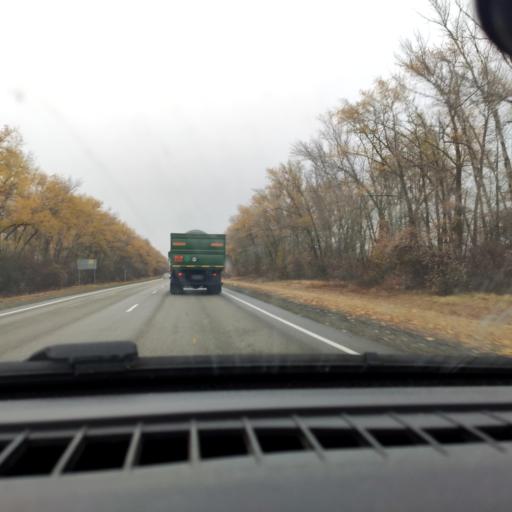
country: RU
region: Voronezj
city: Ostrogozhsk
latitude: 50.9852
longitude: 38.9960
